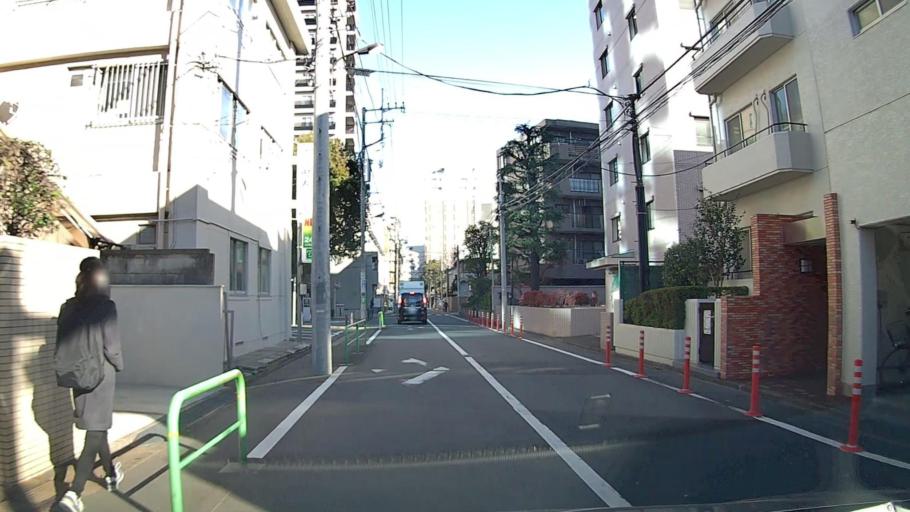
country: JP
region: Tokyo
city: Tokyo
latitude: 35.7349
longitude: 139.6512
